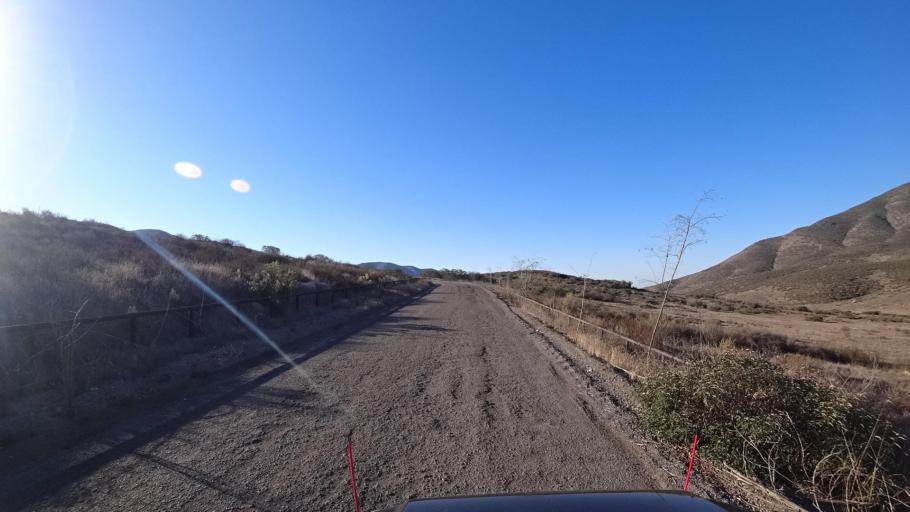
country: US
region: California
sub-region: San Diego County
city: Jamul
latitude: 32.6982
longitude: -116.9051
